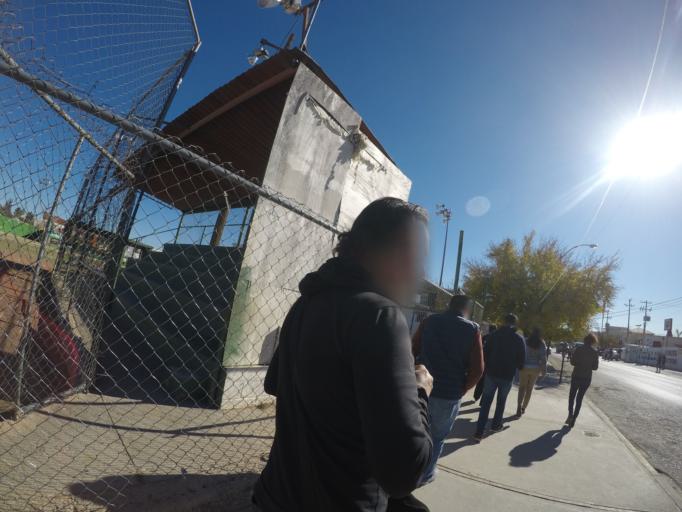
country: MX
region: Chihuahua
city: Ciudad Juarez
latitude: 31.7354
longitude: -106.4622
